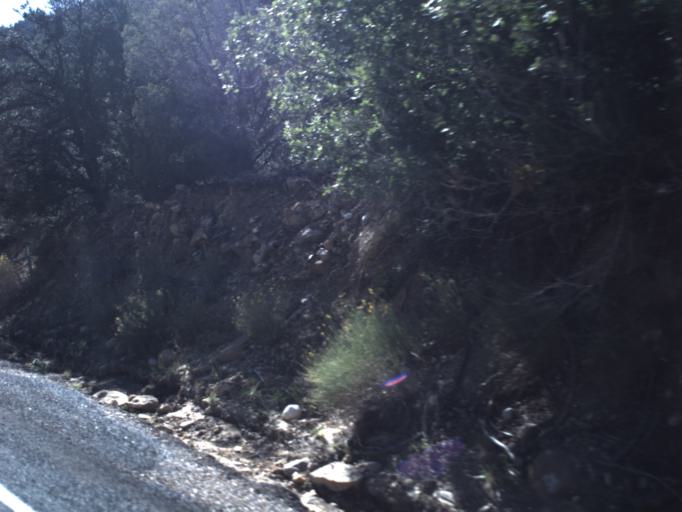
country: US
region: Utah
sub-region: Iron County
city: Parowan
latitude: 37.7989
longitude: -112.8153
